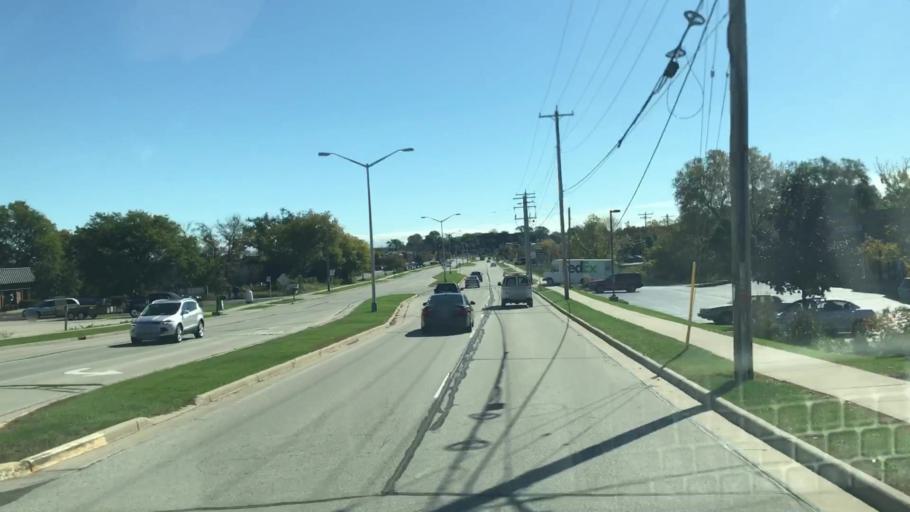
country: US
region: Wisconsin
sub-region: Waukesha County
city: Pewaukee
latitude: 43.0450
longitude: -88.2651
